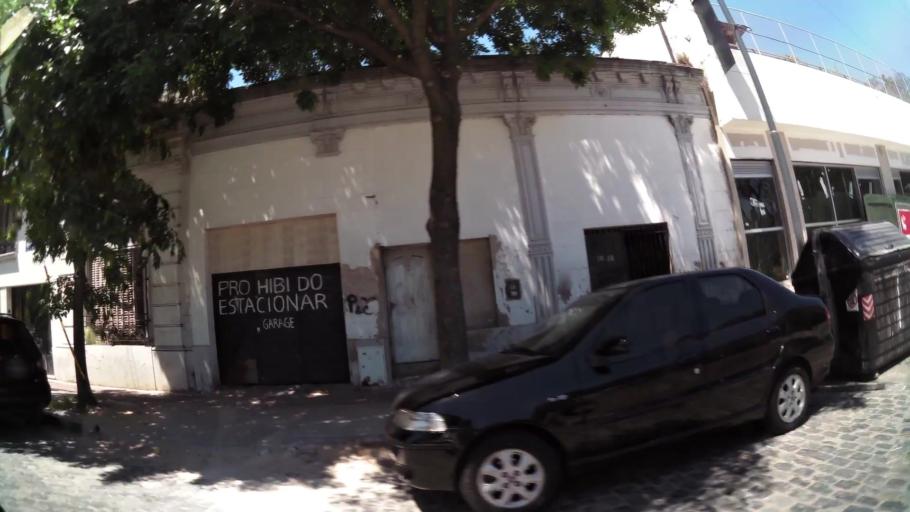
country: AR
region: Buenos Aires F.D.
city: Buenos Aires
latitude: -34.6383
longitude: -58.4051
